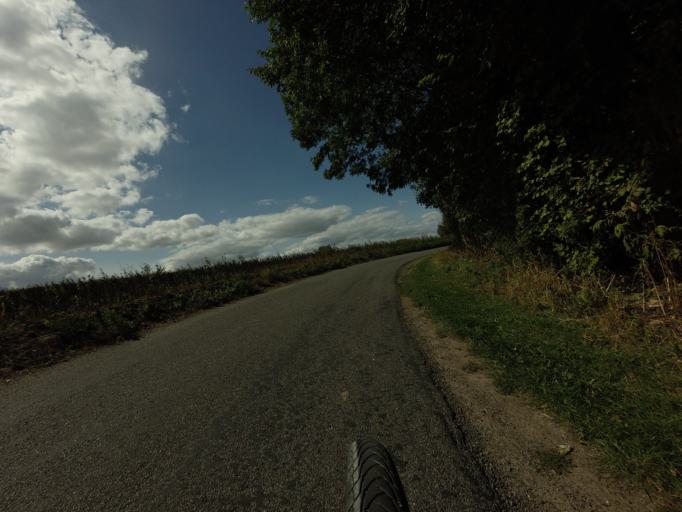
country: DK
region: Zealand
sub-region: Vordingborg Kommune
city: Stege
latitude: 55.0071
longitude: 12.4724
